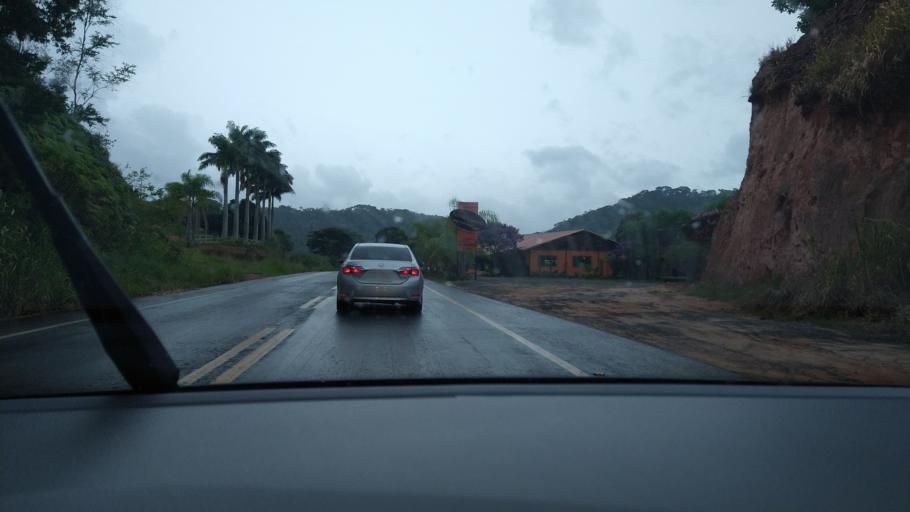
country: BR
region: Minas Gerais
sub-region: Vicosa
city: Vicosa
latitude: -20.6460
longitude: -42.8656
